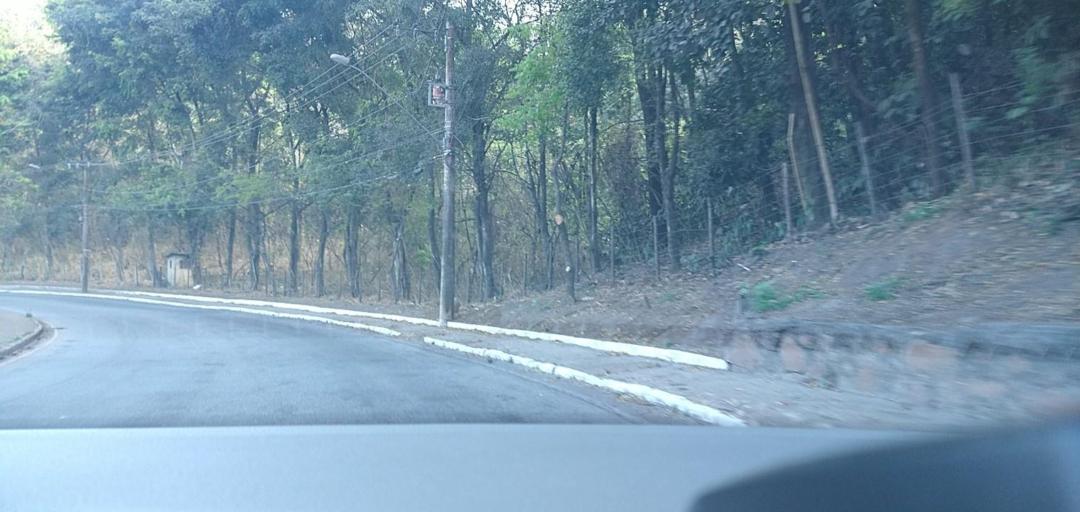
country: BR
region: Minas Gerais
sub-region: Joao Monlevade
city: Joao Monlevade
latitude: -19.8240
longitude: -43.1317
